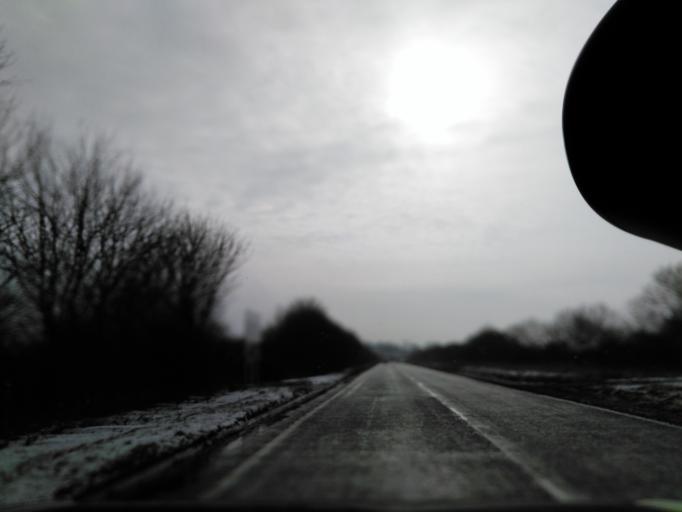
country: GB
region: England
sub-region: Wiltshire
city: Chippenham
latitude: 51.4381
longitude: -2.1377
